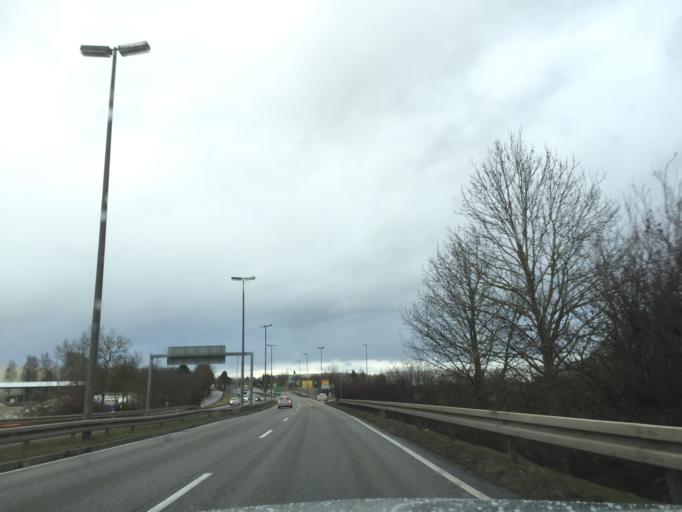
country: DE
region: Baden-Wuerttemberg
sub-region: Regierungsbezirk Stuttgart
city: Boeblingen
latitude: 48.6908
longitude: 8.9792
